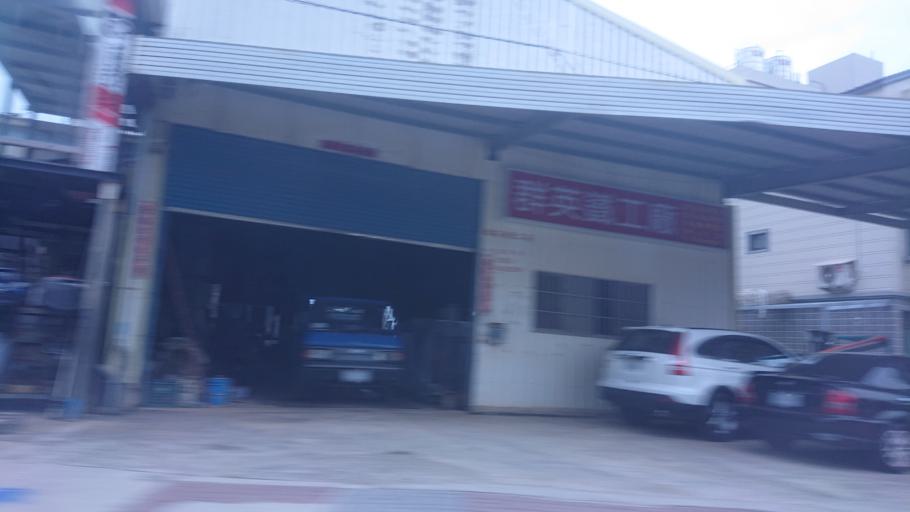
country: TW
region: Fukien
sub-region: Kinmen
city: Jincheng
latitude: 24.4402
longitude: 118.3118
